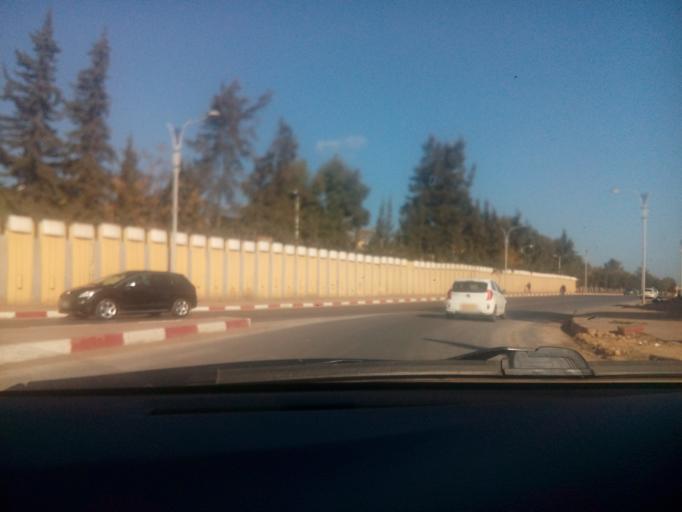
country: DZ
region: Oran
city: Oran
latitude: 35.6803
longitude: -0.6736
